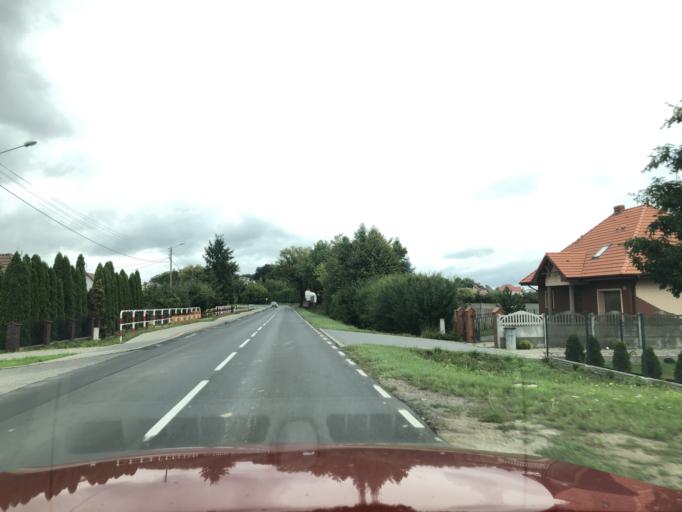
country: PL
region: Greater Poland Voivodeship
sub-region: Powiat szamotulski
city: Wronki
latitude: 52.6885
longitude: 16.3899
